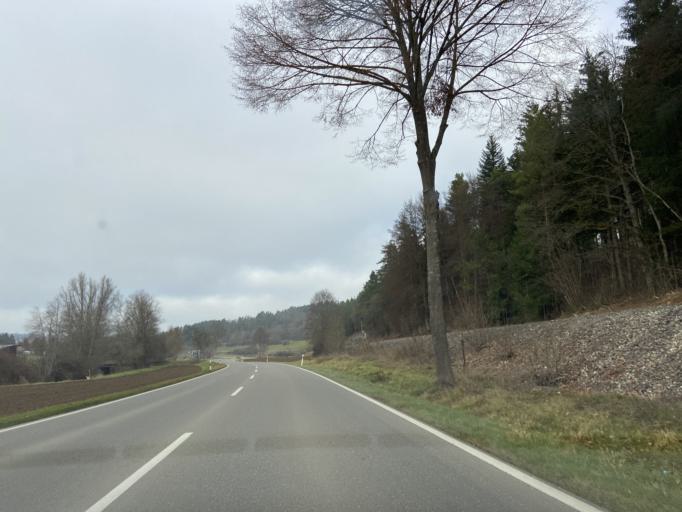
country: DE
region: Baden-Wuerttemberg
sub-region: Tuebingen Region
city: Gammertingen
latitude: 48.2372
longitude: 9.2247
